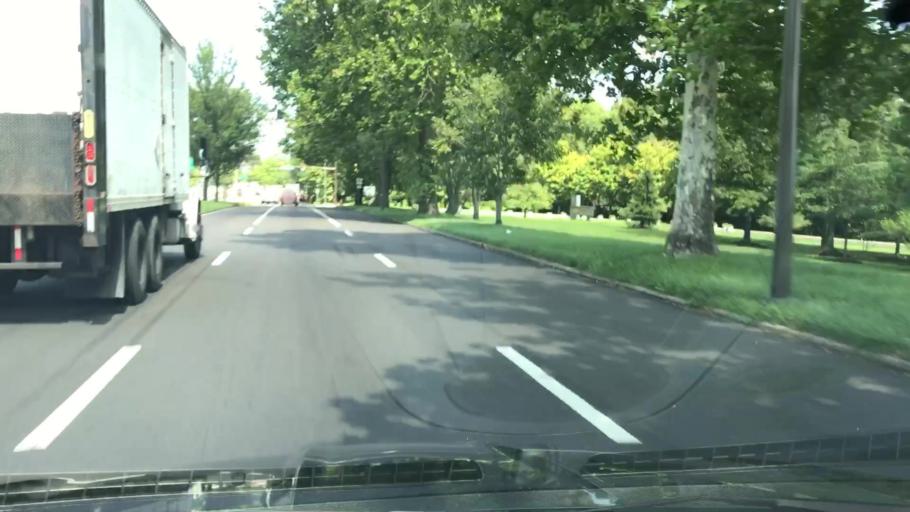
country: US
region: Pennsylvania
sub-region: Bucks County
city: Trevose
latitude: 40.1112
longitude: -74.9917
